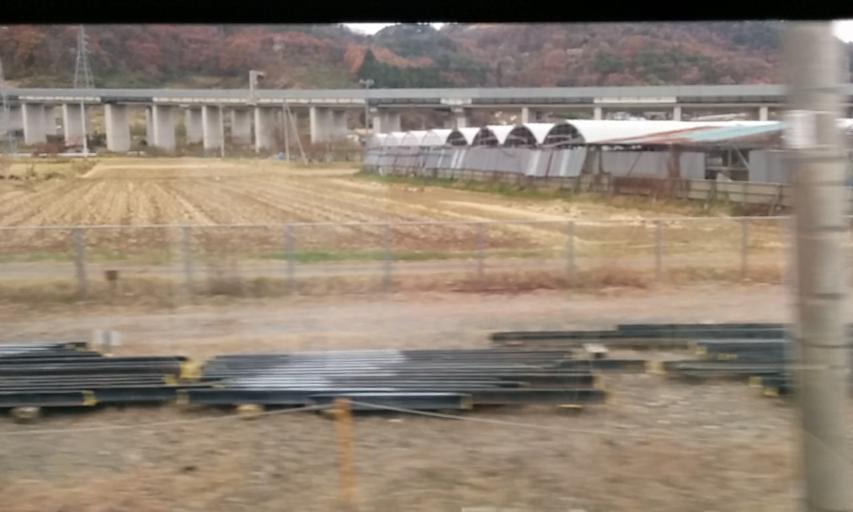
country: JP
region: Nagano
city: Nagano-shi
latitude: 36.5515
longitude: 138.1063
